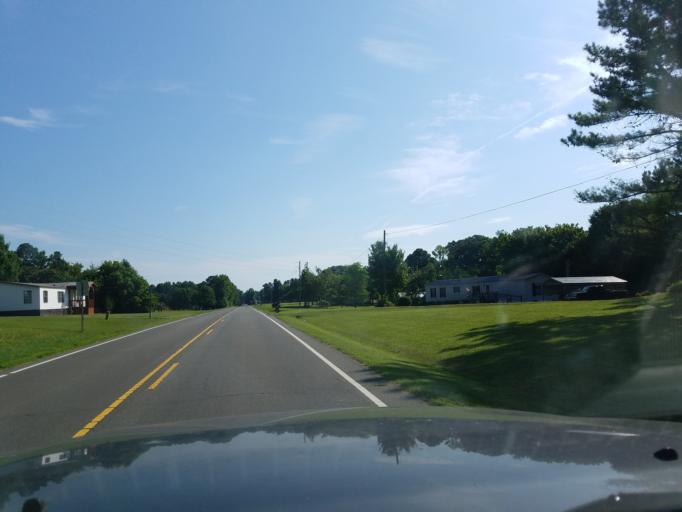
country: US
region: North Carolina
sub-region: Granville County
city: Oxford
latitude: 36.2591
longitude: -78.6566
